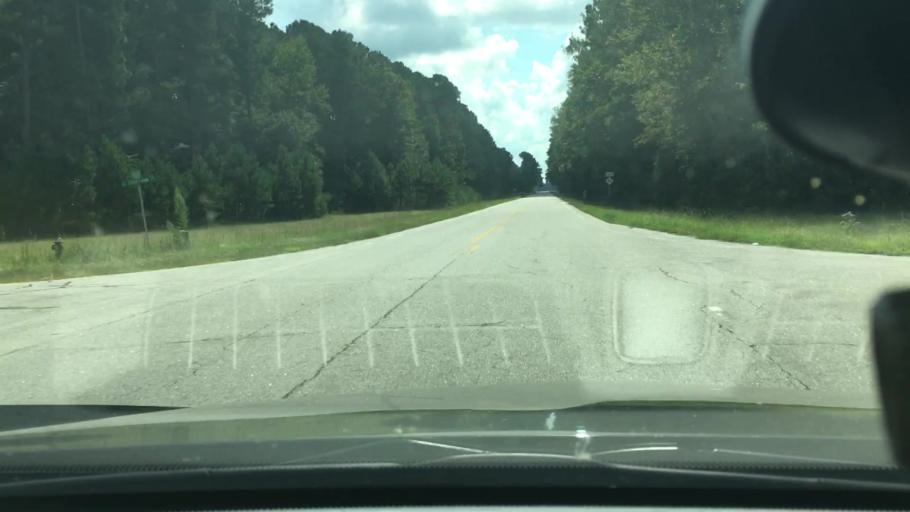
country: US
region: North Carolina
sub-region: Edgecombe County
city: Pinetops
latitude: 35.7610
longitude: -77.5574
